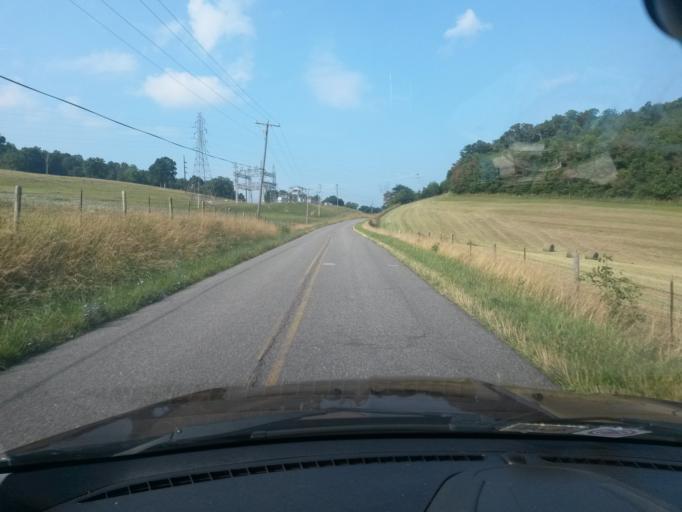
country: US
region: Virginia
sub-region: Giles County
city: Narrows
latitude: 37.3740
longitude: -80.7965
